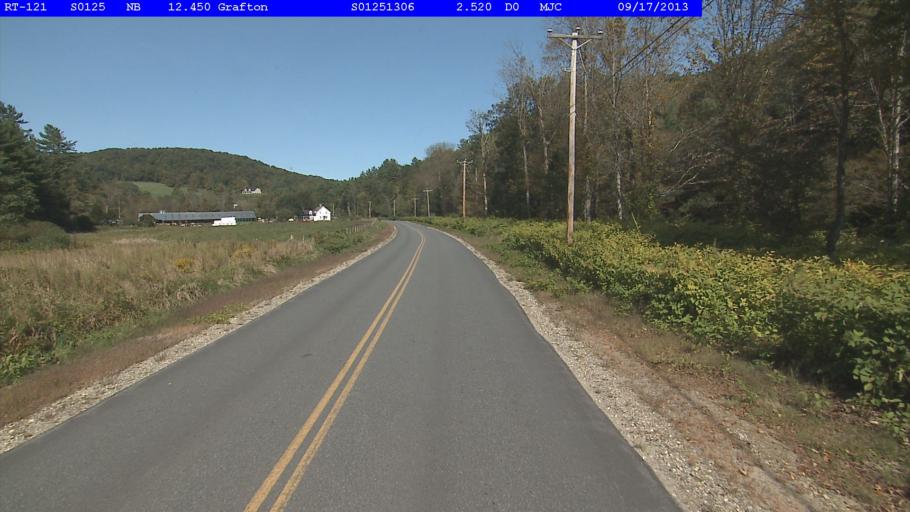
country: US
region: Vermont
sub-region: Windsor County
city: Chester
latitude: 43.1748
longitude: -72.5808
